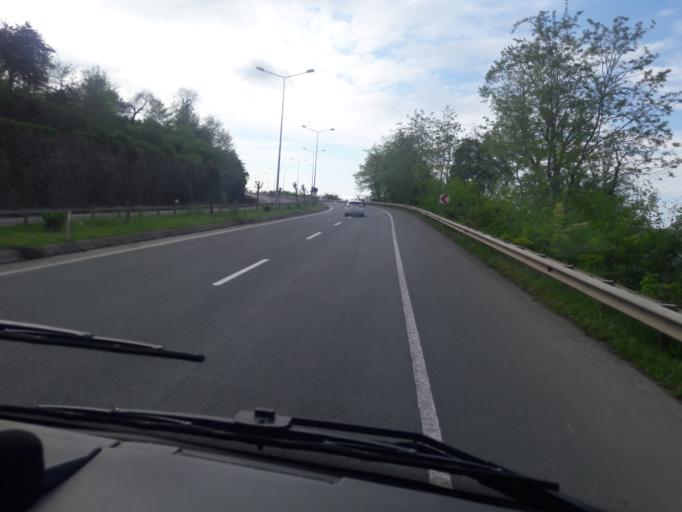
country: TR
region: Giresun
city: Piraziz
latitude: 40.9608
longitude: 38.1046
